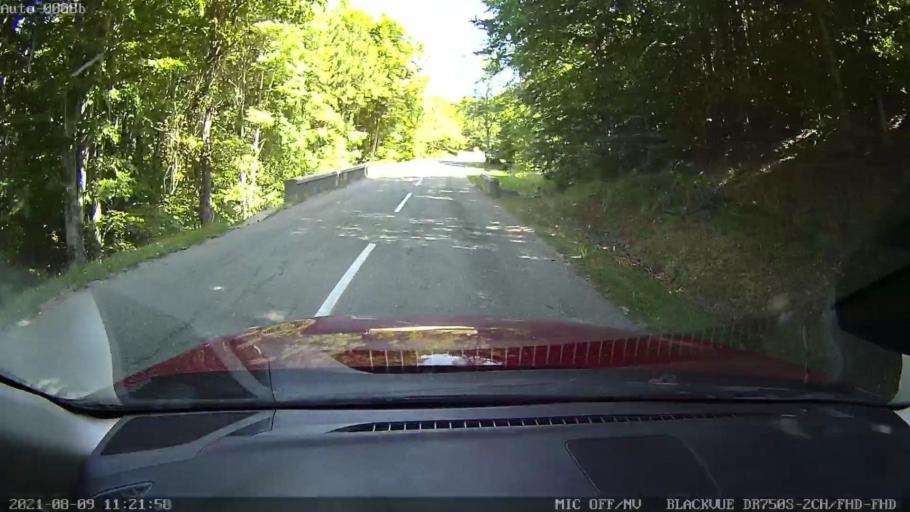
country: HR
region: Istarska
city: Lovran
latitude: 45.3061
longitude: 14.2040
